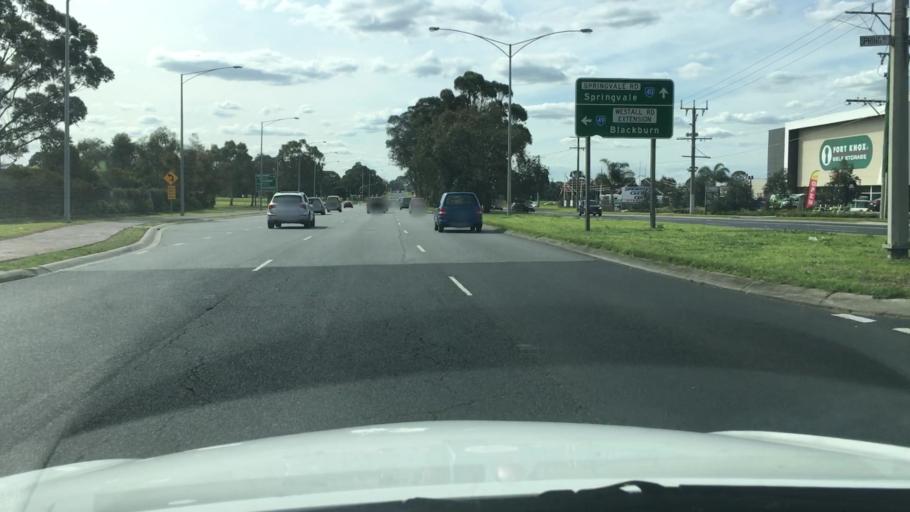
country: AU
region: Victoria
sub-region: Kingston
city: Dingley Village
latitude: -37.9863
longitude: 145.1453
